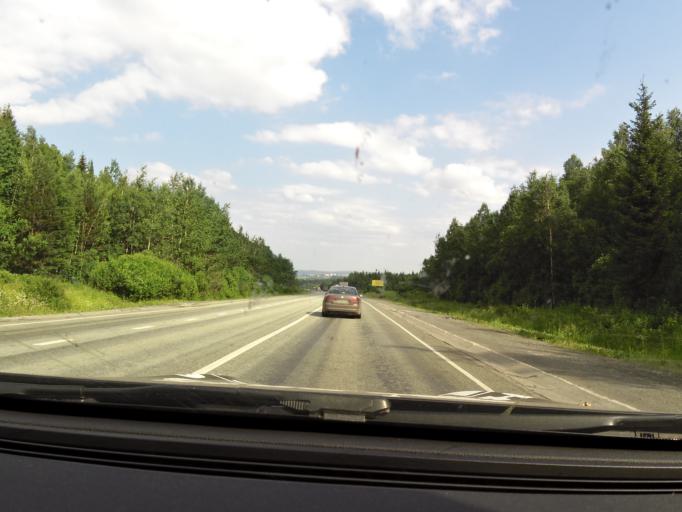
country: RU
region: Sverdlovsk
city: Revda
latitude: 56.8324
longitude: 59.8428
